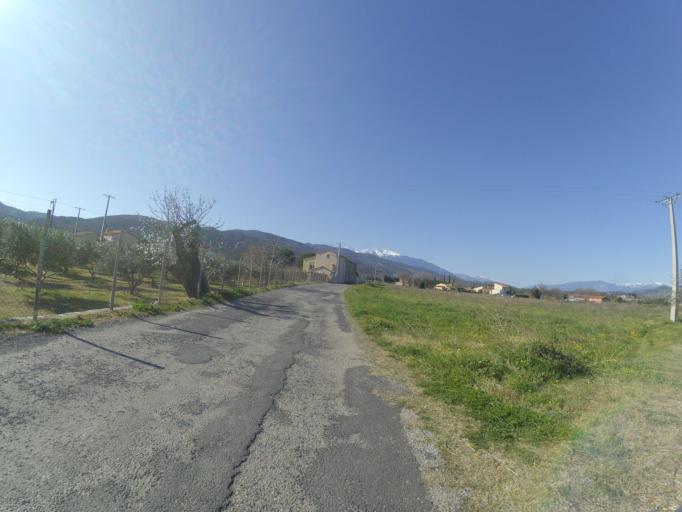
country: FR
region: Languedoc-Roussillon
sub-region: Departement des Pyrenees-Orientales
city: Ille-sur-Tet
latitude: 42.6626
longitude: 2.6134
